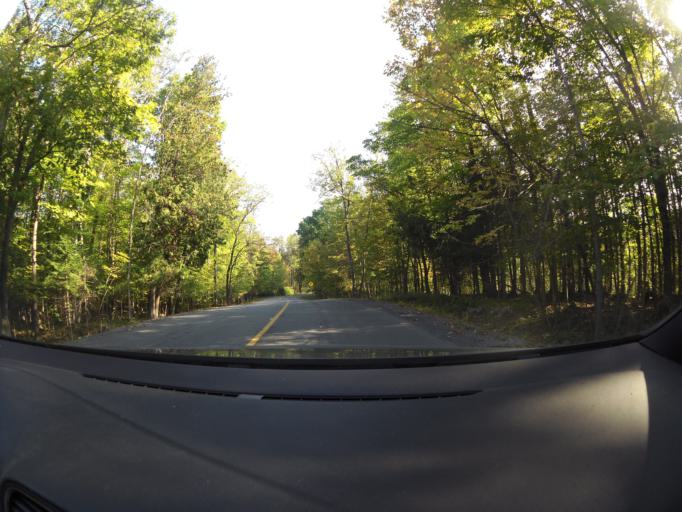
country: CA
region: Ontario
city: Arnprior
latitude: 45.4550
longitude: -76.2753
